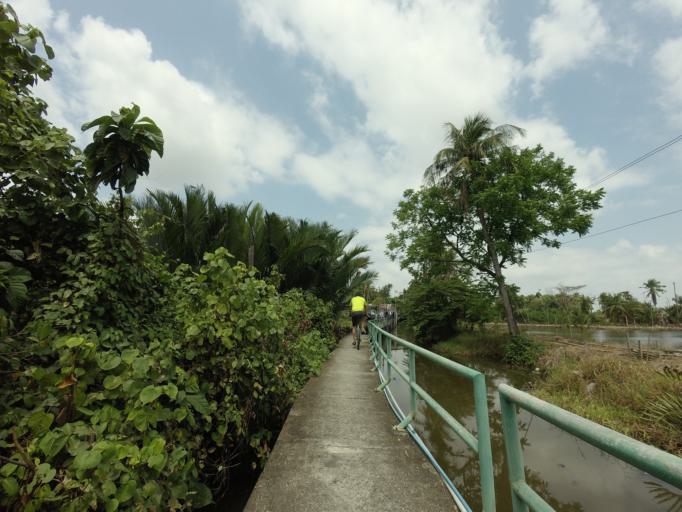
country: TH
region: Bangkok
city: Thung Khru
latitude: 13.6328
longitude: 100.4814
